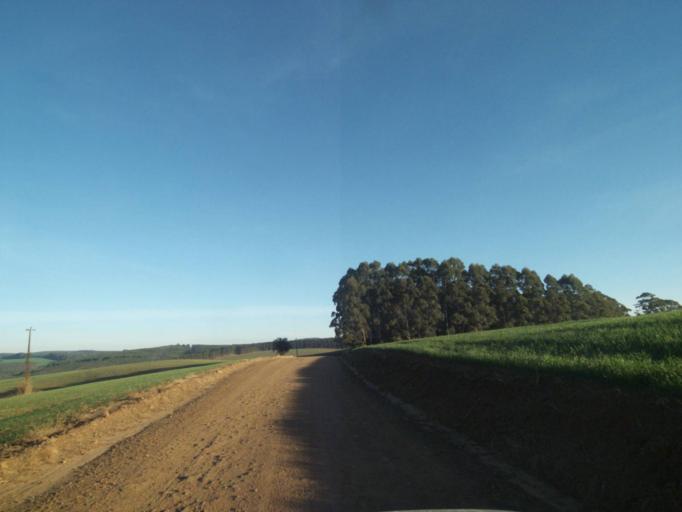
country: BR
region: Parana
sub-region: Telemaco Borba
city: Telemaco Borba
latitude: -24.4760
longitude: -50.5874
